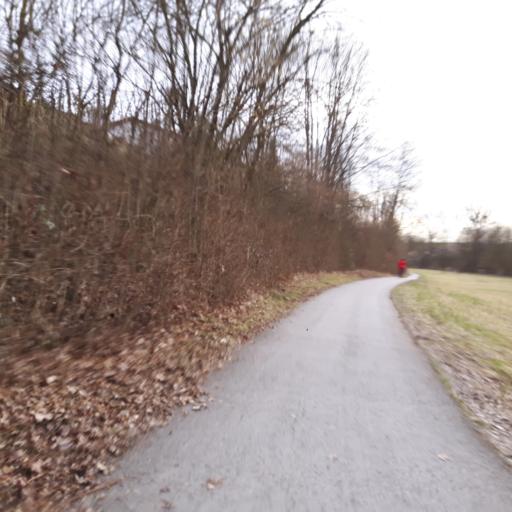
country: DE
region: Baden-Wuerttemberg
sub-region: Regierungsbezirk Stuttgart
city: Grossbottwar
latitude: 48.9849
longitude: 9.2896
